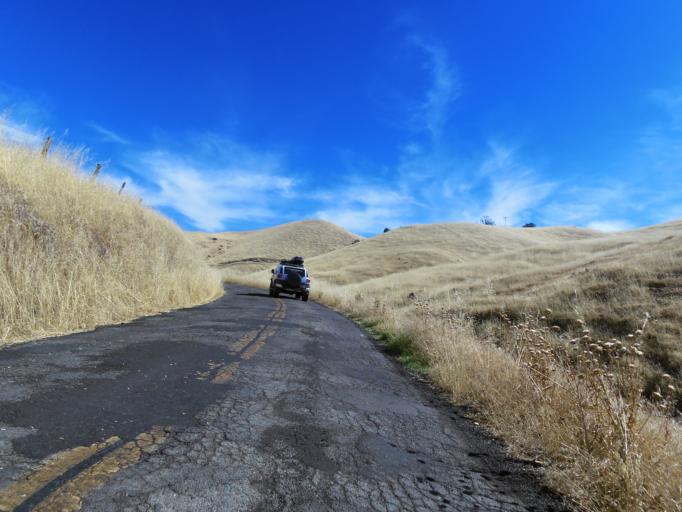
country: US
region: California
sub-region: Mariposa County
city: Mariposa
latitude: 37.3308
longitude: -119.9665
